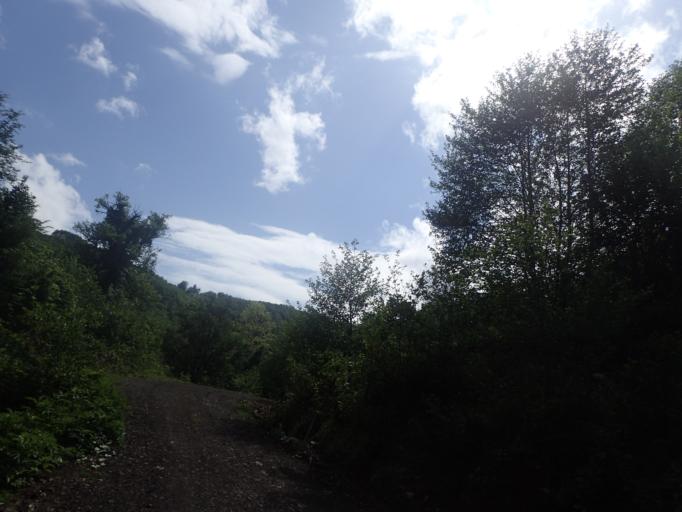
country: TR
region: Ordu
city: Akkus
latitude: 40.9058
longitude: 36.8800
